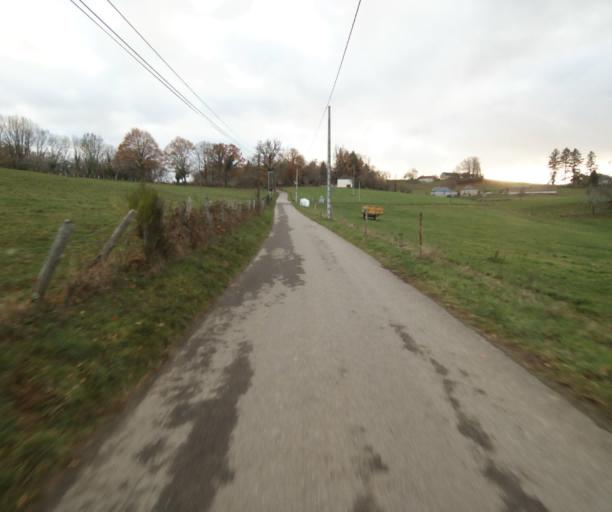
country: FR
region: Limousin
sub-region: Departement de la Correze
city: Laguenne
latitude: 45.2259
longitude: 1.7826
